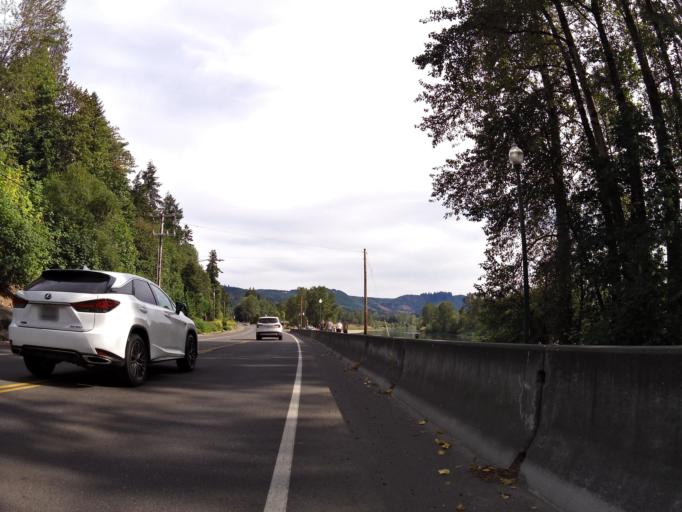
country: US
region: Washington
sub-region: Cowlitz County
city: Castle Rock
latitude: 46.2672
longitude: -122.9044
